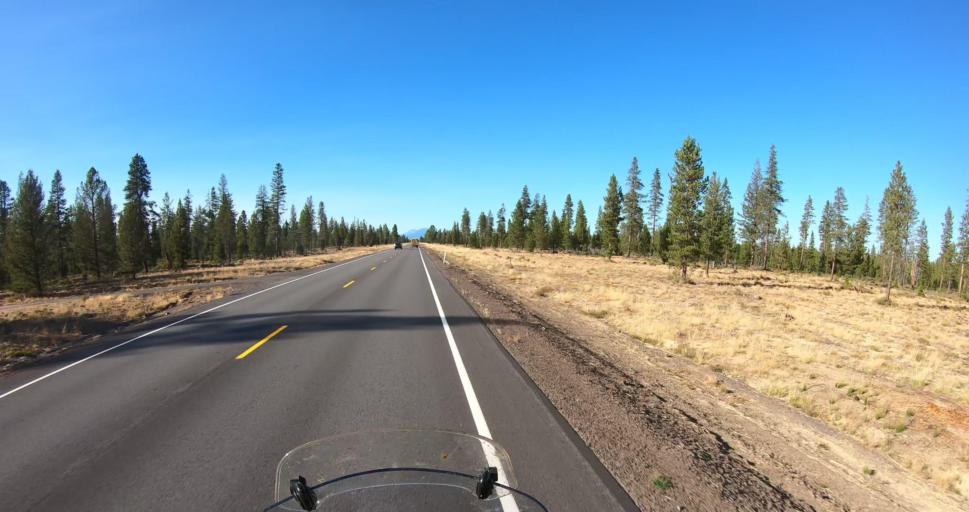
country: US
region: Oregon
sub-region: Deschutes County
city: La Pine
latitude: 43.5880
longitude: -121.4912
